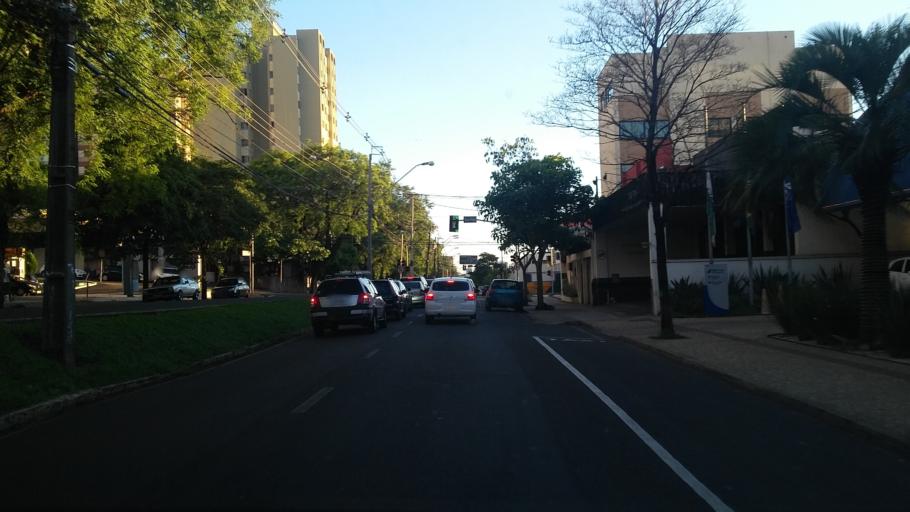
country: BR
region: Parana
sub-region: Londrina
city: Londrina
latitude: -23.3137
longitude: -51.1706
